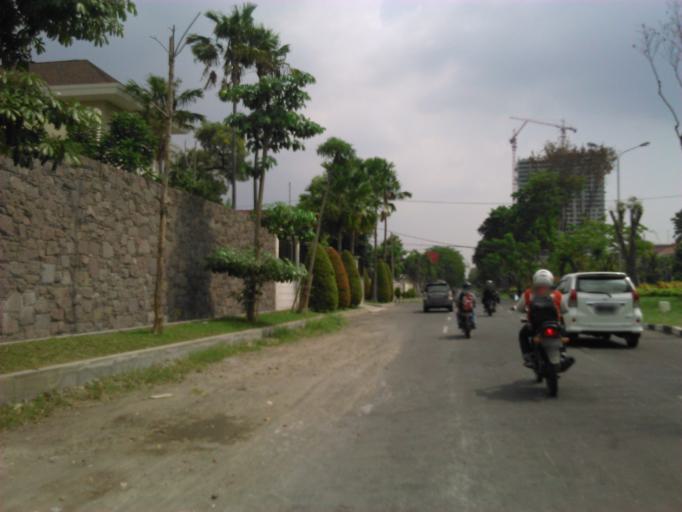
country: ID
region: East Java
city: Mulyorejo
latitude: -7.2800
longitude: 112.7864
